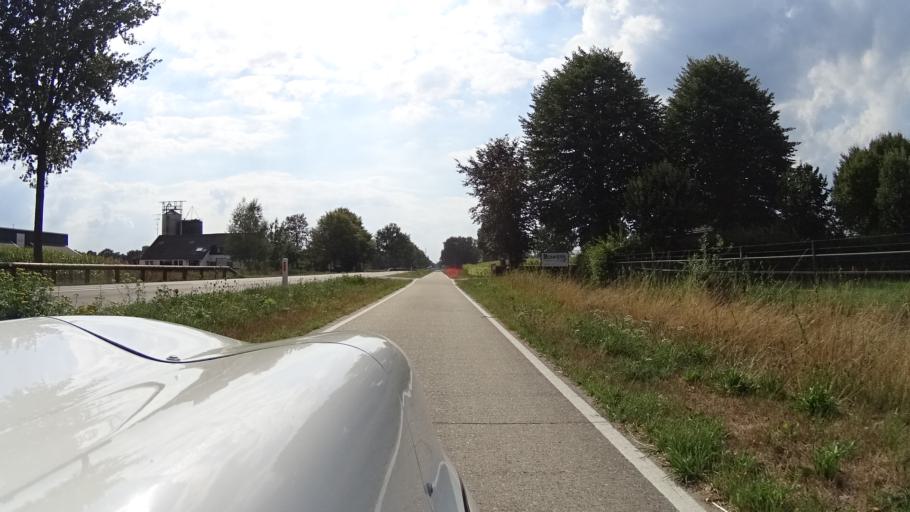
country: NL
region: North Brabant
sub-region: Gemeente Mill en Sint Hubert
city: Wilbertoord
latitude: 51.5815
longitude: 5.7844
